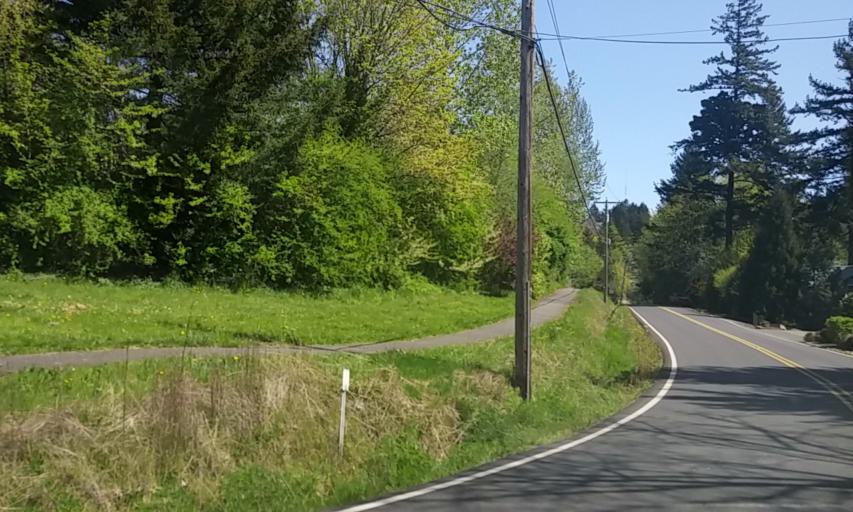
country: US
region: Oregon
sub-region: Washington County
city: West Haven
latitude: 45.5209
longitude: -122.7721
